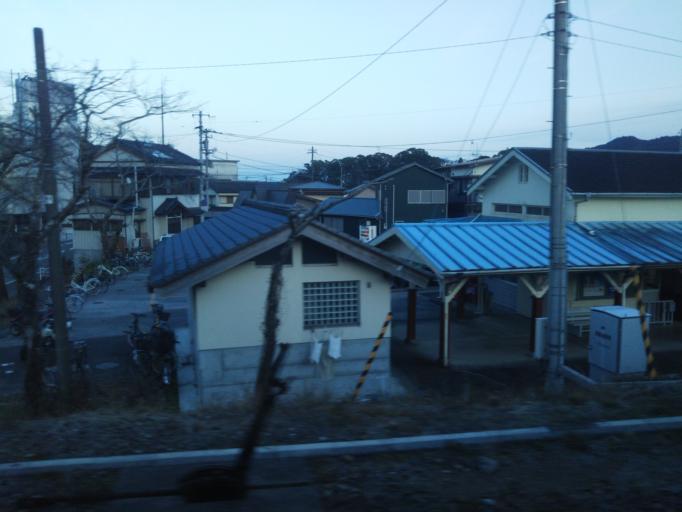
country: JP
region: Kochi
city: Susaki
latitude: 33.3302
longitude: 133.2270
